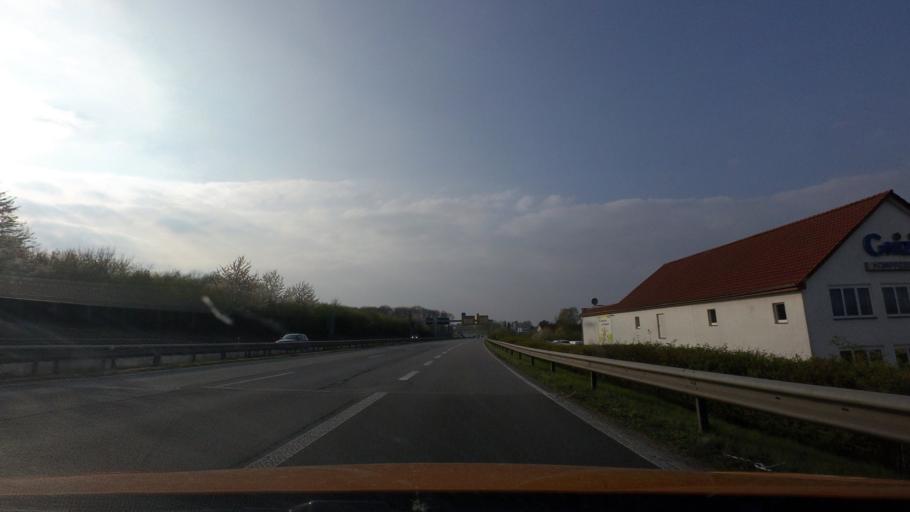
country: DE
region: North Rhine-Westphalia
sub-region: Regierungsbezirk Detmold
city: Herford
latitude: 52.0906
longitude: 8.6935
